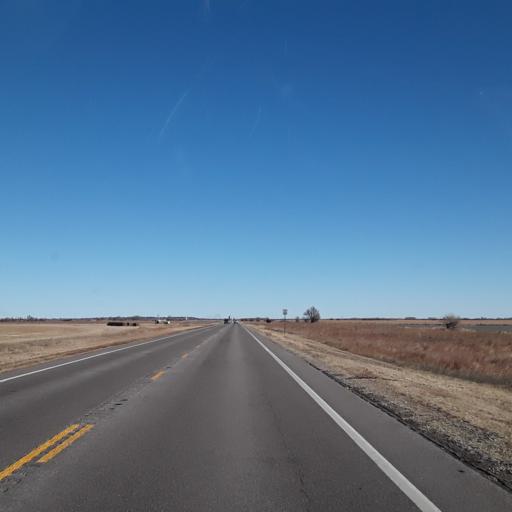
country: US
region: Kansas
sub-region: Pawnee County
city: Larned
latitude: 38.1314
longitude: -99.1628
